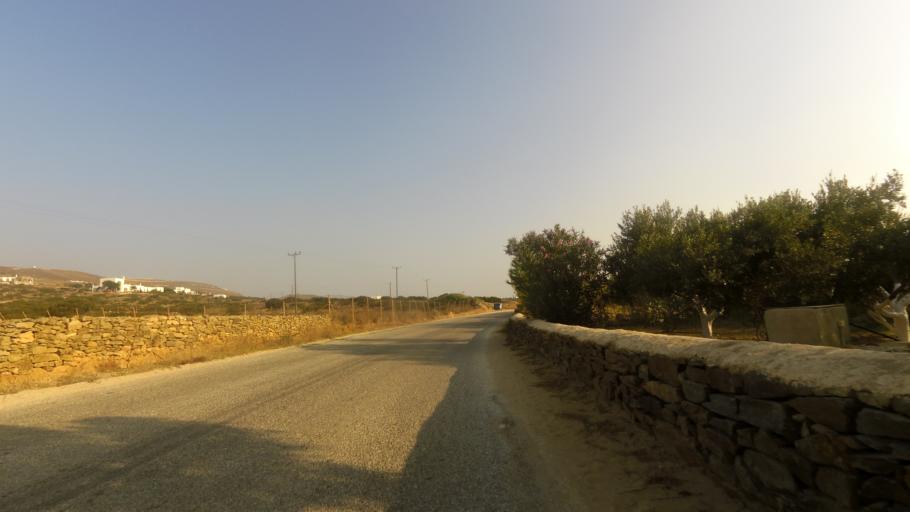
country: GR
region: South Aegean
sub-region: Nomos Kykladon
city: Antiparos
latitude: 37.0241
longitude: 25.0765
